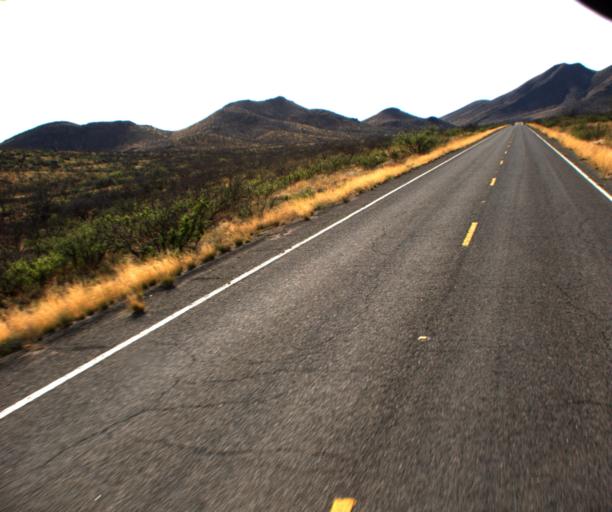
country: US
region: Arizona
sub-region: Cochise County
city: Willcox
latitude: 32.1783
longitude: -109.6287
